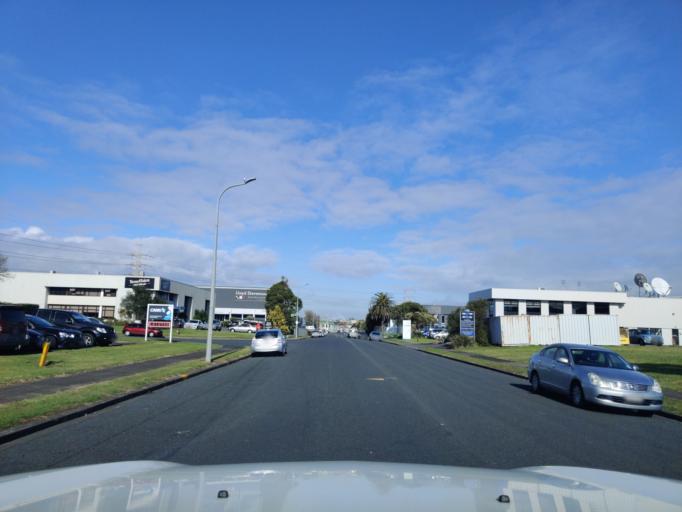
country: NZ
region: Auckland
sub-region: Auckland
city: Manukau City
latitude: -36.9384
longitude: 174.8823
